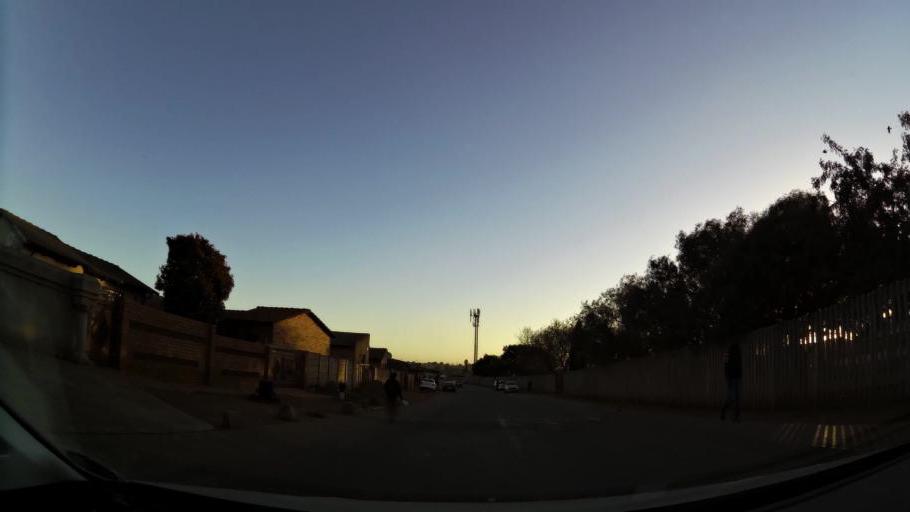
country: ZA
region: Gauteng
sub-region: Ekurhuleni Metropolitan Municipality
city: Tembisa
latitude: -25.9923
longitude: 28.2209
